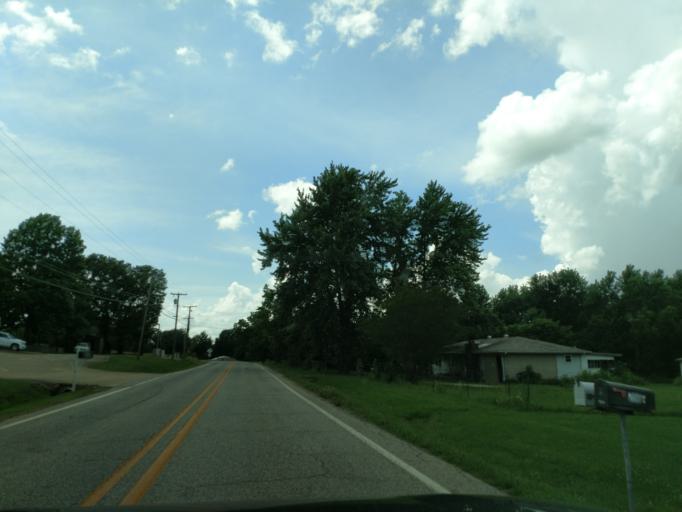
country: US
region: Arkansas
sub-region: Boone County
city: Harrison
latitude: 36.2509
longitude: -93.2163
